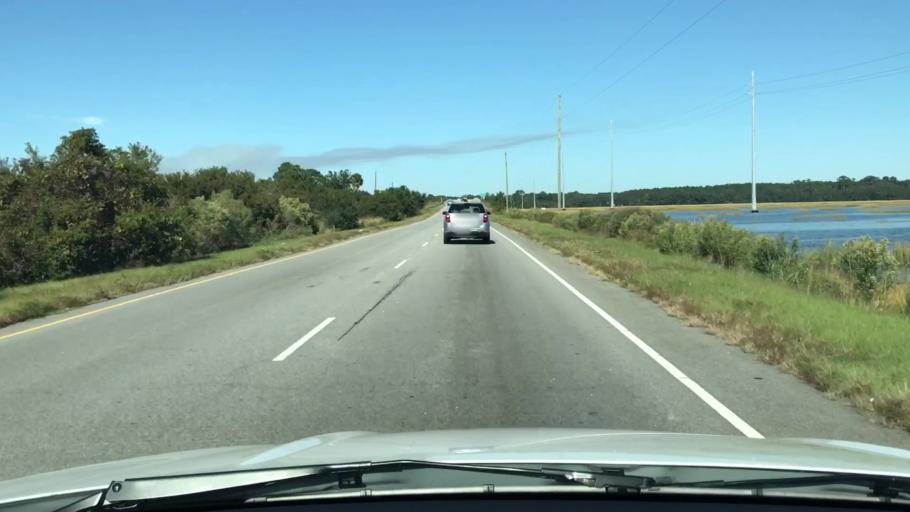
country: US
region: South Carolina
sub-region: Beaufort County
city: Laurel Bay
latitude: 32.5359
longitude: -80.7461
